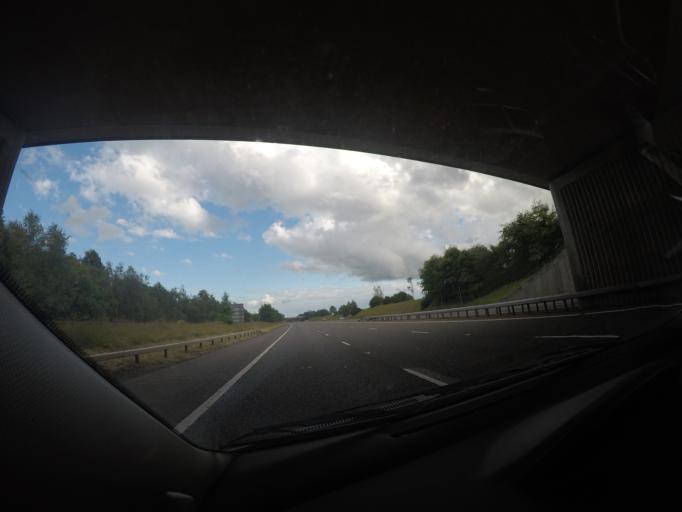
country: GB
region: Scotland
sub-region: Dumfries and Galloway
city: Lockerbie
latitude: 55.1189
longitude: -3.3616
